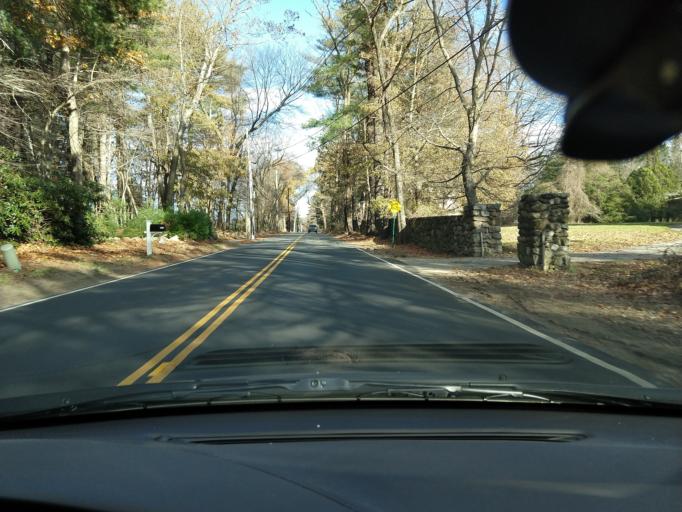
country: US
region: Massachusetts
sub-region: Middlesex County
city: Concord
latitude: 42.4432
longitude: -71.3654
